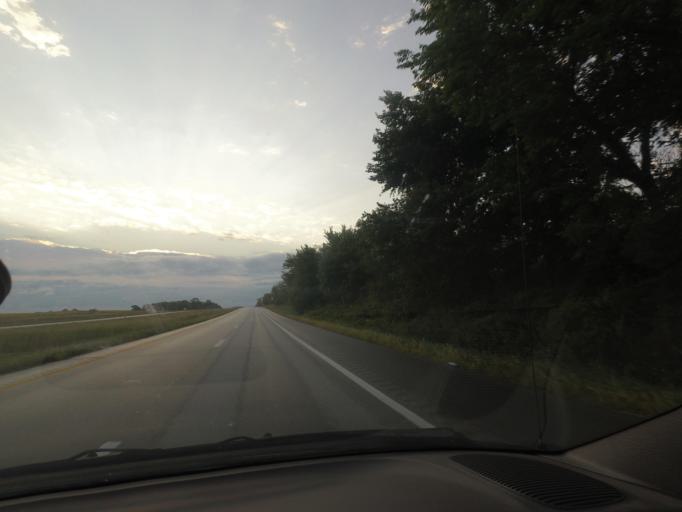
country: US
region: Missouri
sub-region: Shelby County
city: Shelbina
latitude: 39.7207
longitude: -92.1559
